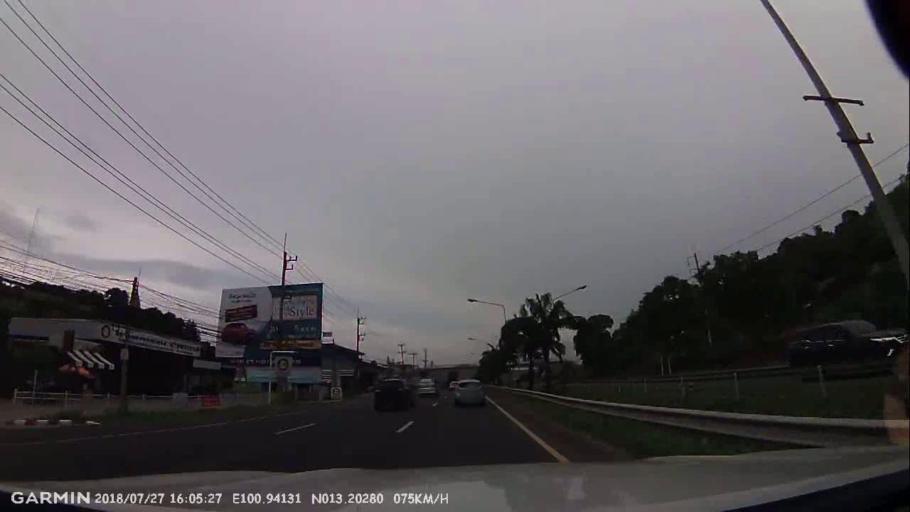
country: TH
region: Chon Buri
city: Si Racha
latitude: 13.2029
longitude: 100.9414
